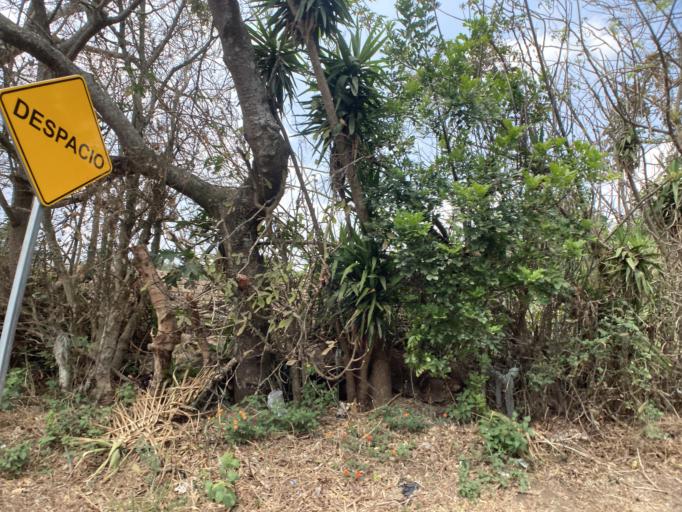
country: GT
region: Escuintla
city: San Vicente Pacaya
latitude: 14.3469
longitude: -90.5713
